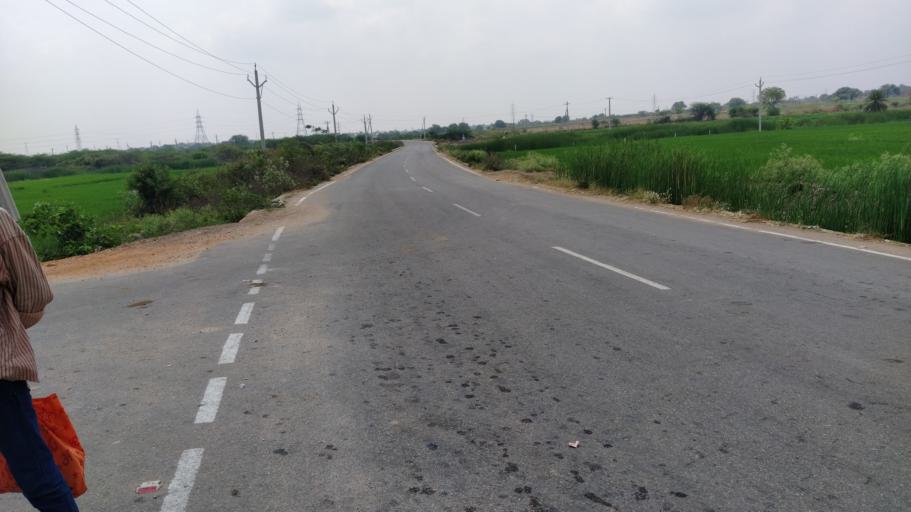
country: IN
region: Telangana
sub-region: Mahbubnagar
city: Nagar Karnul
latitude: 16.4979
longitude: 78.3669
